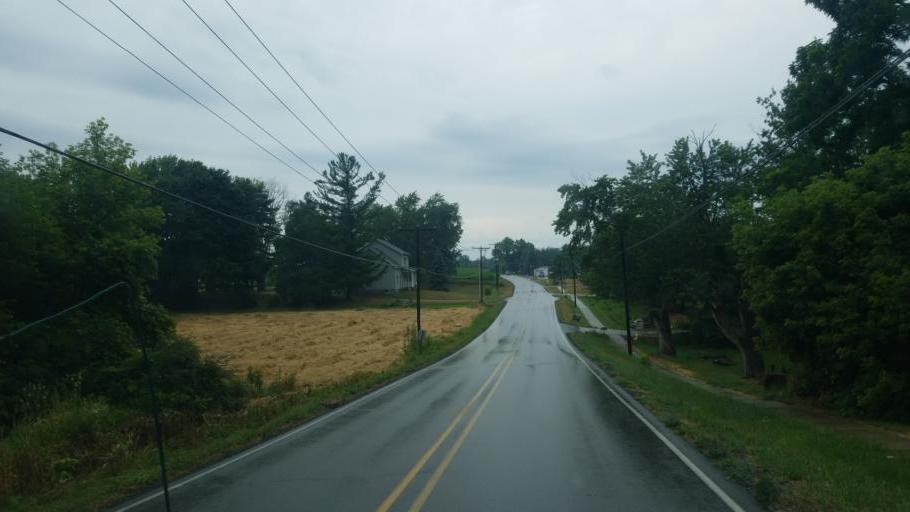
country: US
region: Indiana
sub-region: Steuben County
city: Hamilton
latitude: 41.5357
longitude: -84.9218
